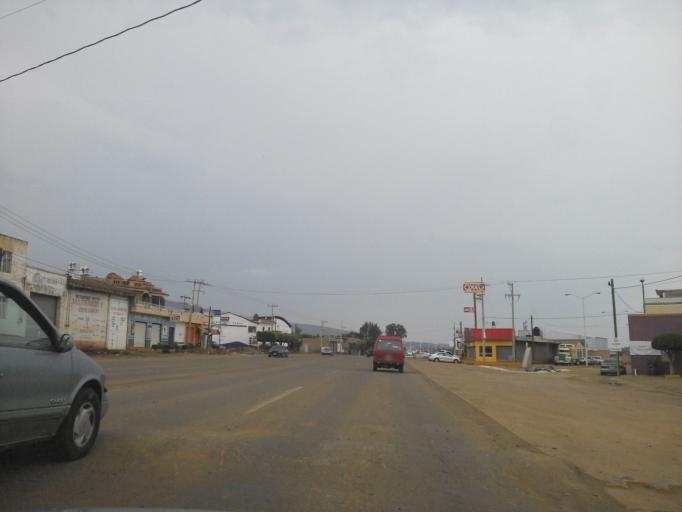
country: MX
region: Jalisco
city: San Jose de Gracia
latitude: 20.7477
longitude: -102.5375
